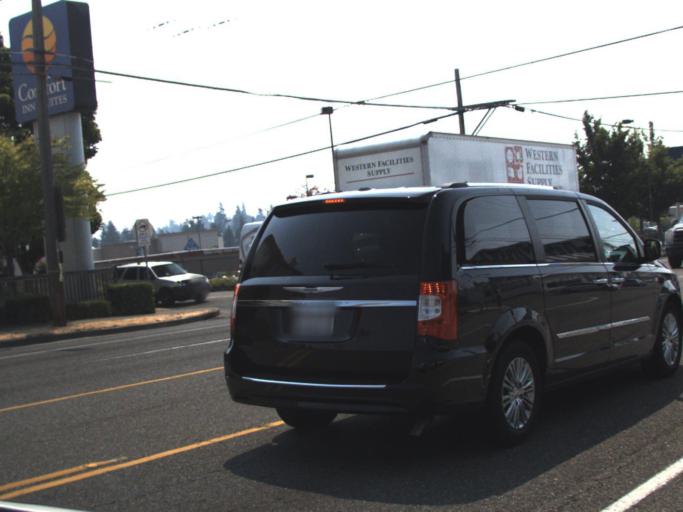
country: US
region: Washington
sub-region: King County
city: Shoreline
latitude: 47.7288
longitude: -122.3450
